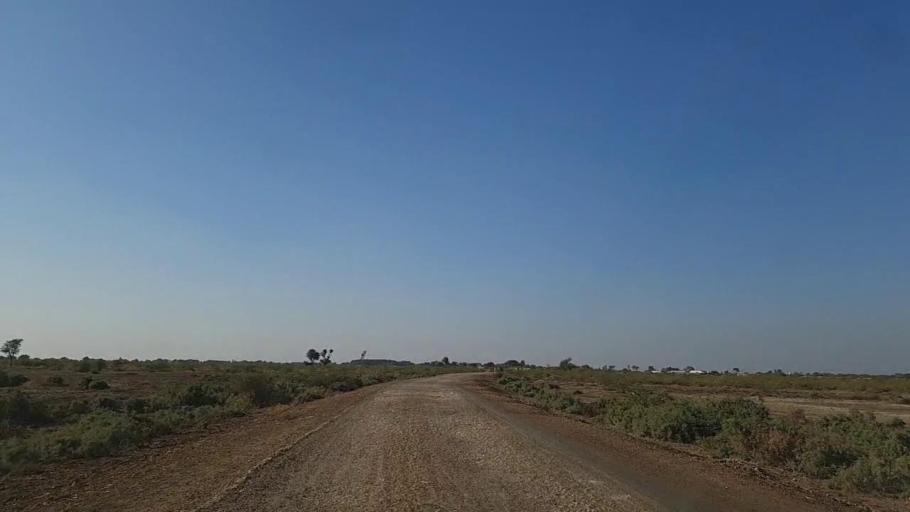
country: PK
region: Sindh
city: Samaro
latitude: 25.3565
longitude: 69.3771
